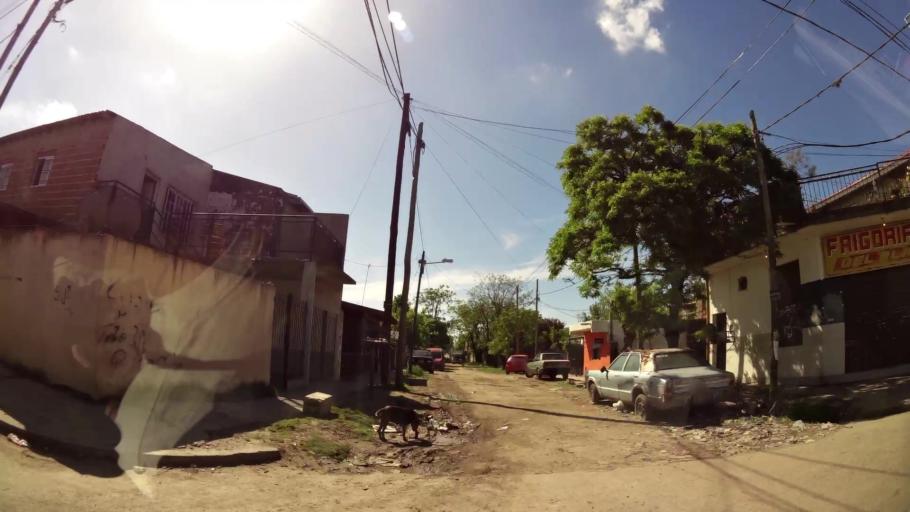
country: AR
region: Buenos Aires
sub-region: Partido de Quilmes
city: Quilmes
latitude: -34.7958
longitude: -58.2516
